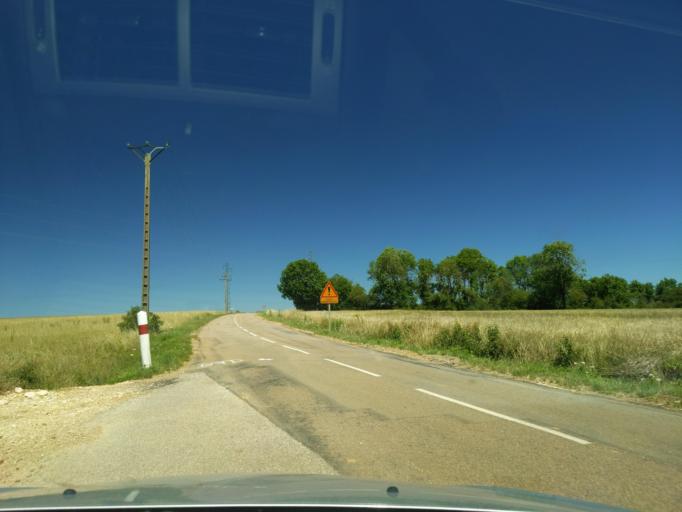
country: FR
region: Bourgogne
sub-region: Departement de la Cote-d'Or
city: Saint-Julien
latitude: 47.4452
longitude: 5.0903
